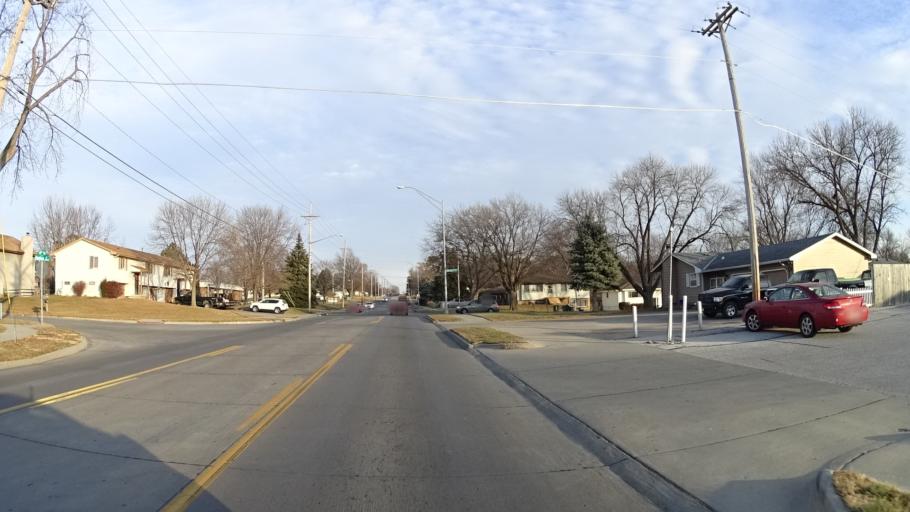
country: US
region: Nebraska
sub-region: Sarpy County
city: La Vista
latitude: 41.1907
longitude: -95.9941
